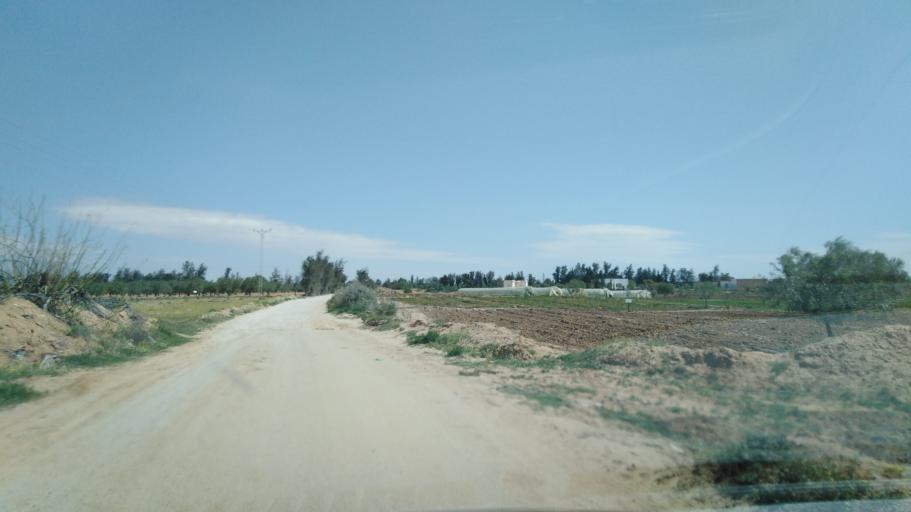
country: TN
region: Safaqis
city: Sfax
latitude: 34.7541
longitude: 10.5287
